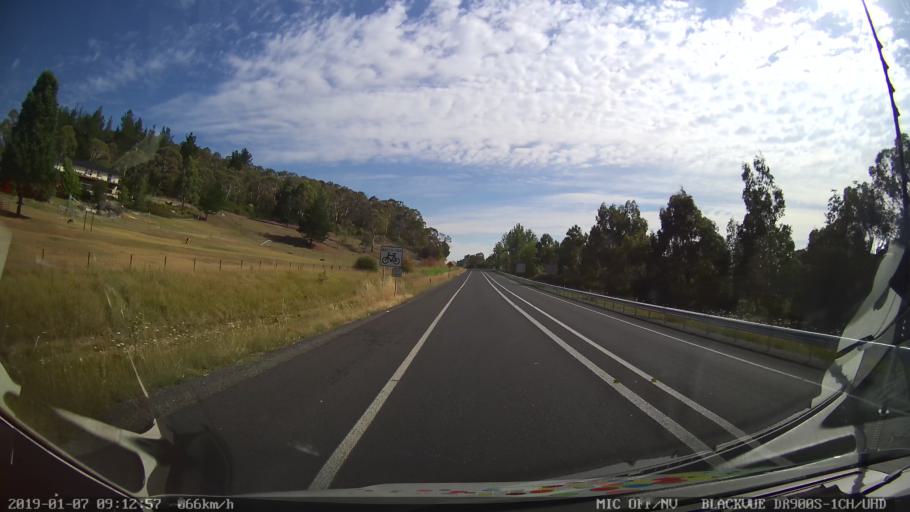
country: AU
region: New South Wales
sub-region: Armidale Dumaresq
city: Armidale
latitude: -30.6369
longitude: 151.5062
